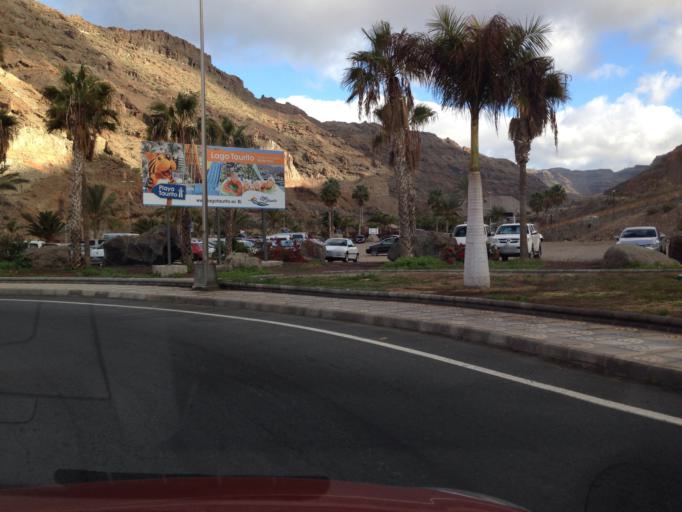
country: ES
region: Canary Islands
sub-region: Provincia de Las Palmas
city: Puerto Rico
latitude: 27.8197
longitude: -15.7504
